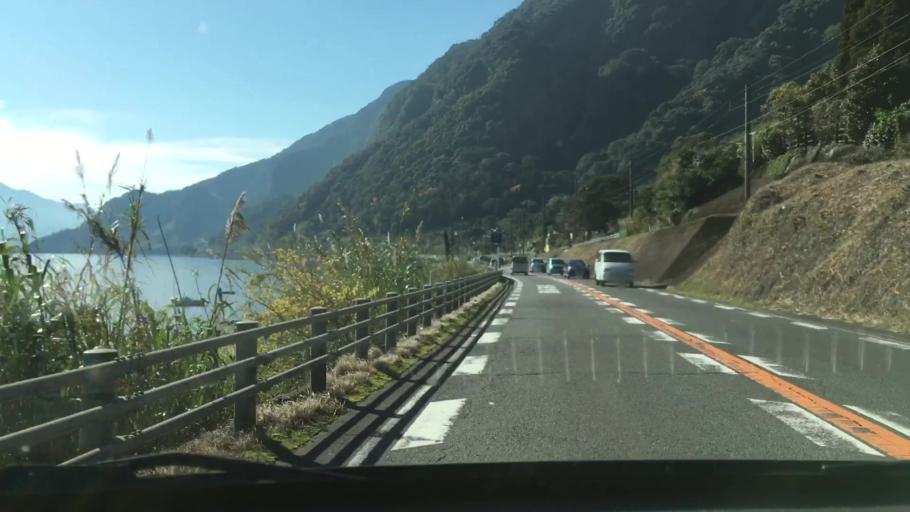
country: JP
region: Kagoshima
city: Kajiki
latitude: 31.6844
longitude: 130.6098
